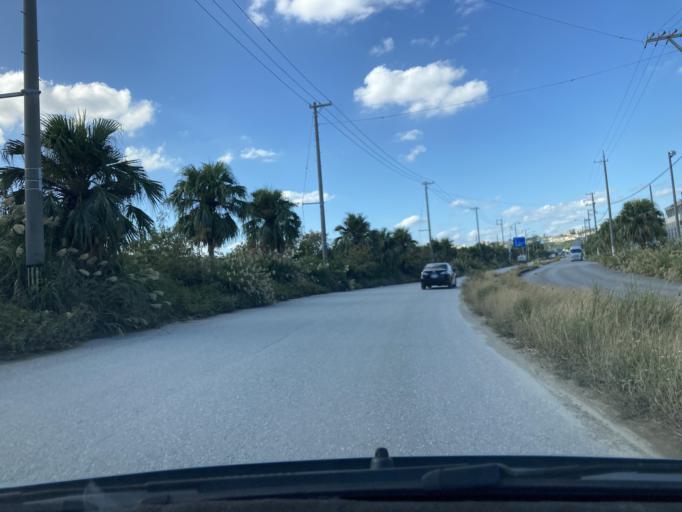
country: JP
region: Okinawa
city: Katsuren-haebaru
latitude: 26.3278
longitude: 127.8438
